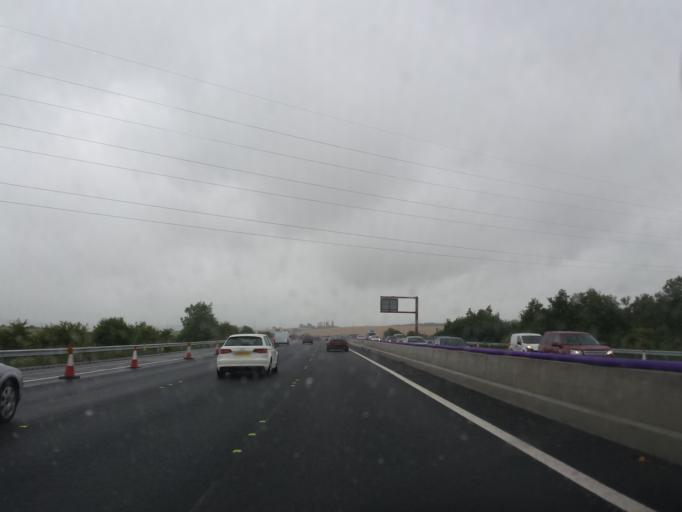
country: GB
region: England
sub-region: Derbyshire
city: Bolsover
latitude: 53.2298
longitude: -1.3325
